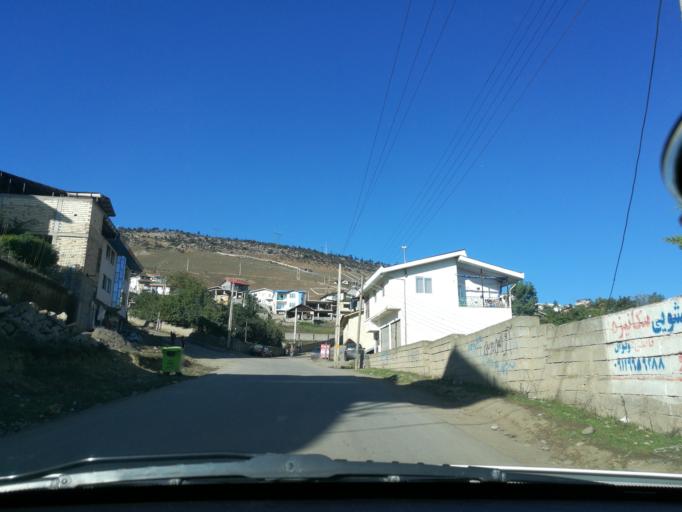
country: IR
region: Mazandaran
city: `Abbasabad
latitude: 36.5548
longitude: 51.1930
